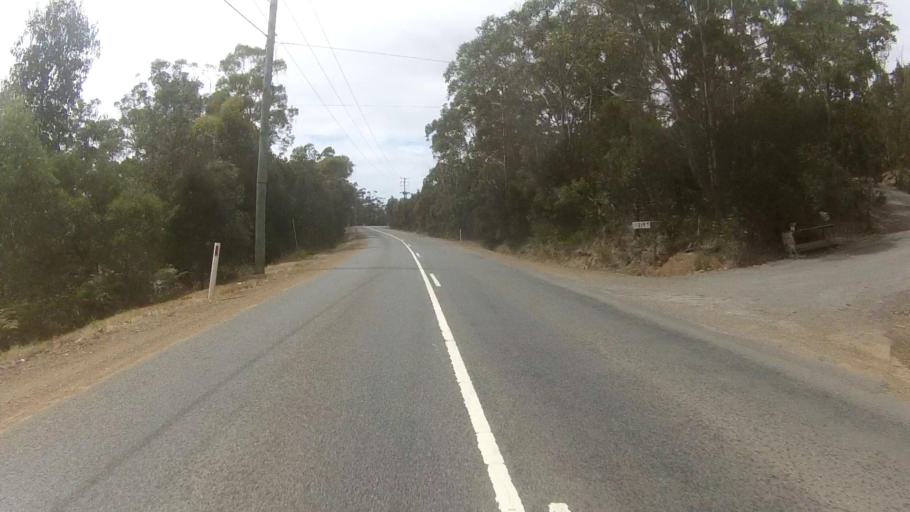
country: AU
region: Tasmania
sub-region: Kingborough
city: Margate
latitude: -43.0052
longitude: 147.2390
